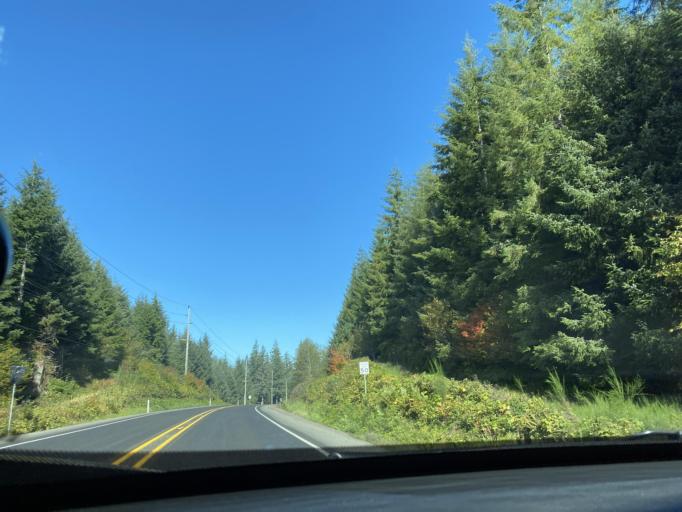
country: US
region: Washington
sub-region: Clallam County
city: Forks
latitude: 47.9649
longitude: -124.4019
